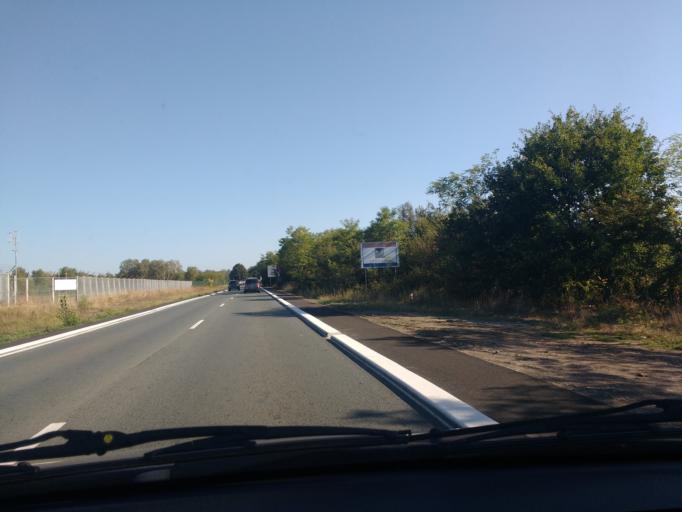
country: FR
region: Aquitaine
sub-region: Departement de la Gironde
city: Le Haillan
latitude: 44.8436
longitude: -0.6927
